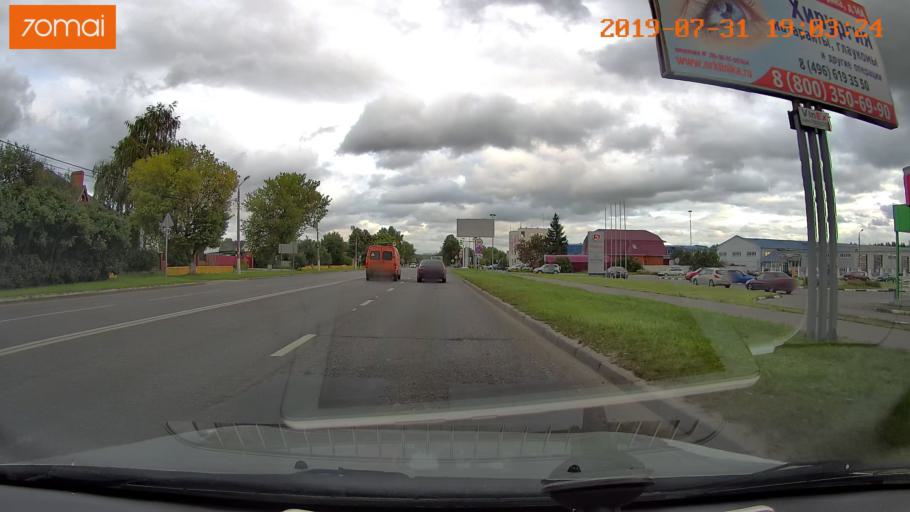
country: RU
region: Moskovskaya
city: Raduzhnyy
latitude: 55.1148
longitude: 38.7372
